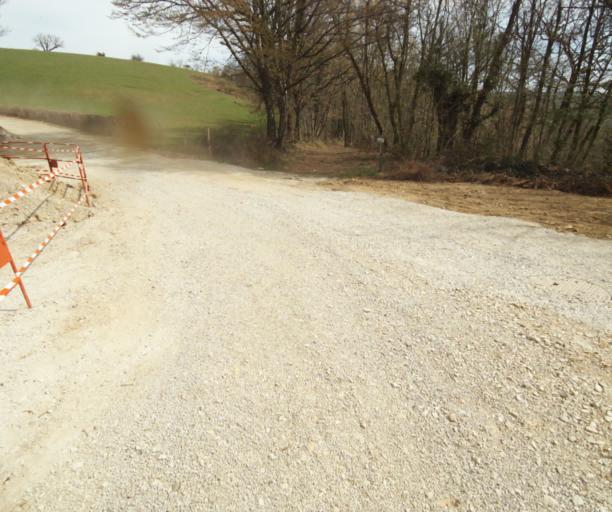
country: FR
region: Limousin
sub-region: Departement de la Correze
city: Naves
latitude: 45.2927
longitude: 1.7786
